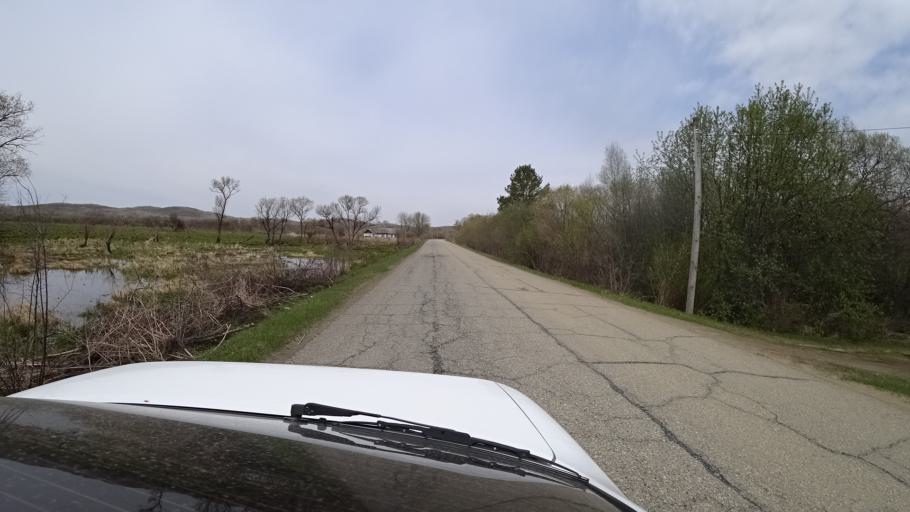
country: RU
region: Primorskiy
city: Novopokrovka
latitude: 45.7831
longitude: 134.1177
